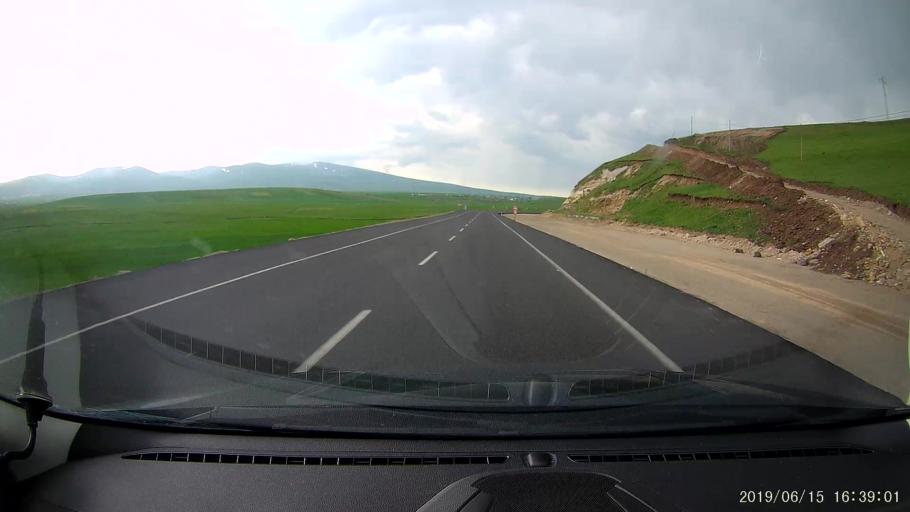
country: TR
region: Ardahan
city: Haskoy
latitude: 40.9873
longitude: 42.8933
